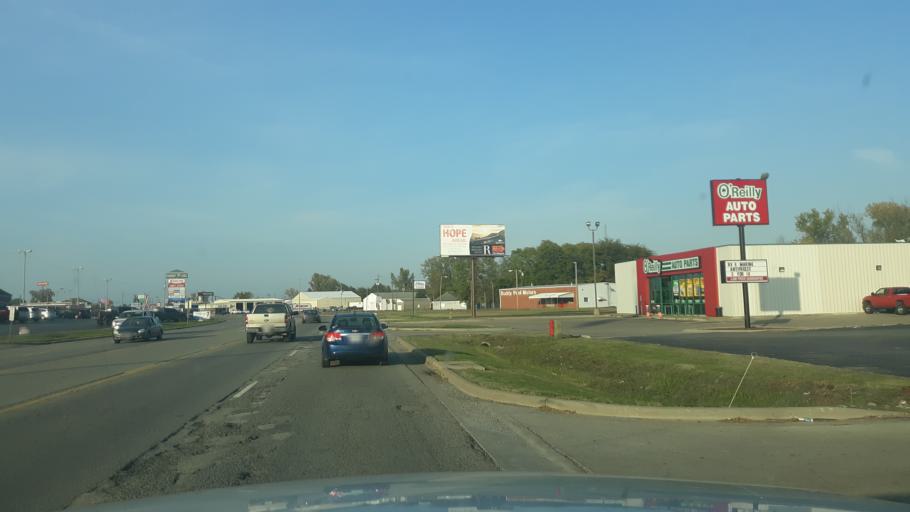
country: US
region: Illinois
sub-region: Saline County
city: Harrisburg
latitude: 37.7332
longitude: -88.5341
